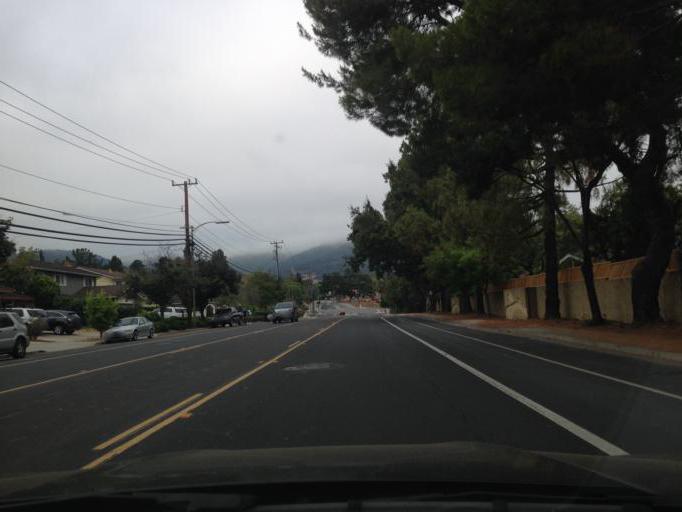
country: US
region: California
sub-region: Santa Clara County
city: Cambrian Park
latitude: 37.2274
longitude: -121.9015
